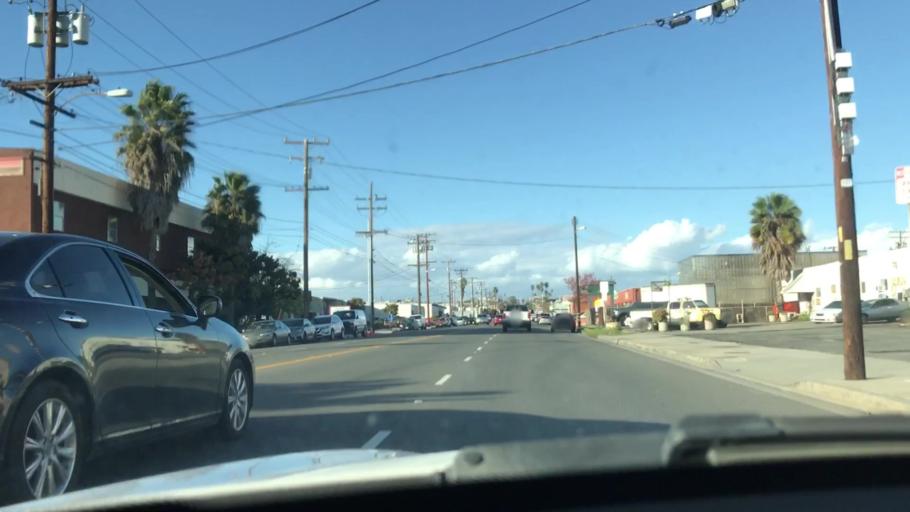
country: US
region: California
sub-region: Los Angeles County
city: West Athens
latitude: 33.9064
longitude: -118.3004
